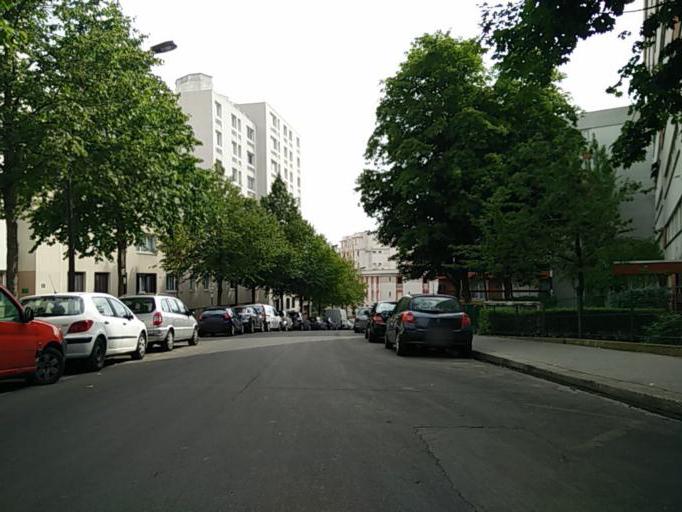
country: FR
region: Ile-de-France
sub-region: Departement de Seine-Saint-Denis
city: Le Pre-Saint-Gervais
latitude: 48.8791
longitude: 2.3985
